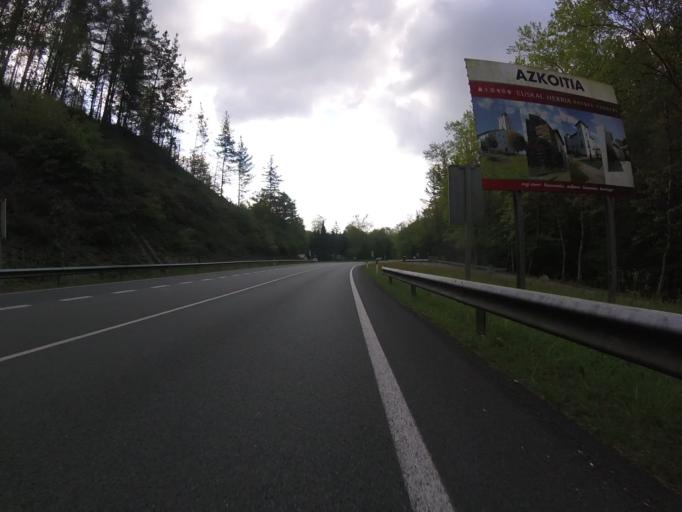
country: ES
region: Basque Country
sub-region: Provincia de Guipuzcoa
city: Azkoitia
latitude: 43.1891
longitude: -2.3293
